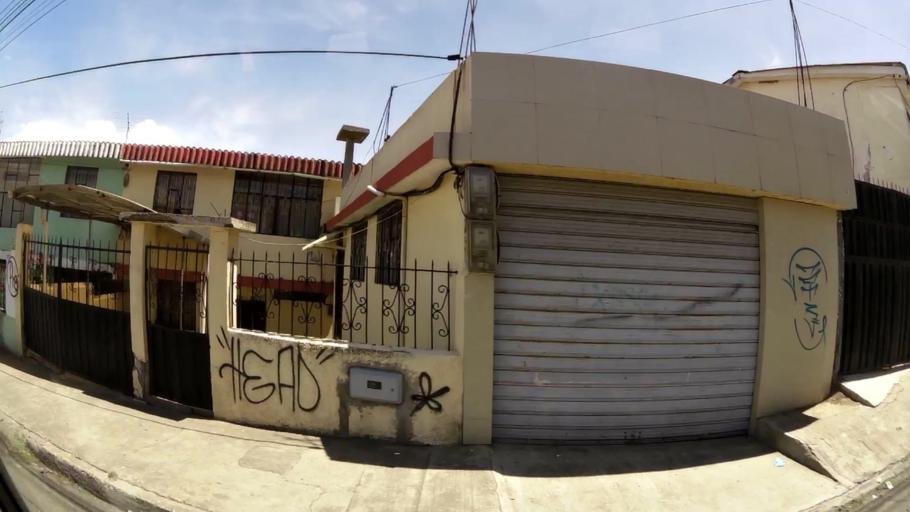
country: EC
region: Chimborazo
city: Riobamba
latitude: -1.6613
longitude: -78.6575
